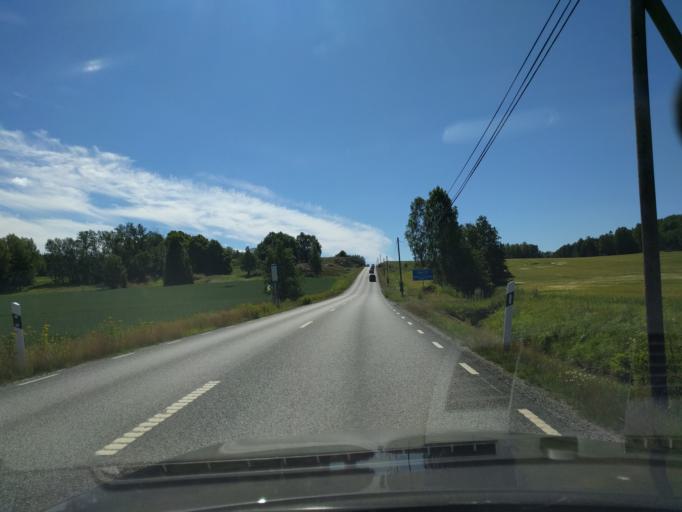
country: SE
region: Stockholm
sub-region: Haninge Kommun
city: Haninge
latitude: 59.1400
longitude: 18.1859
